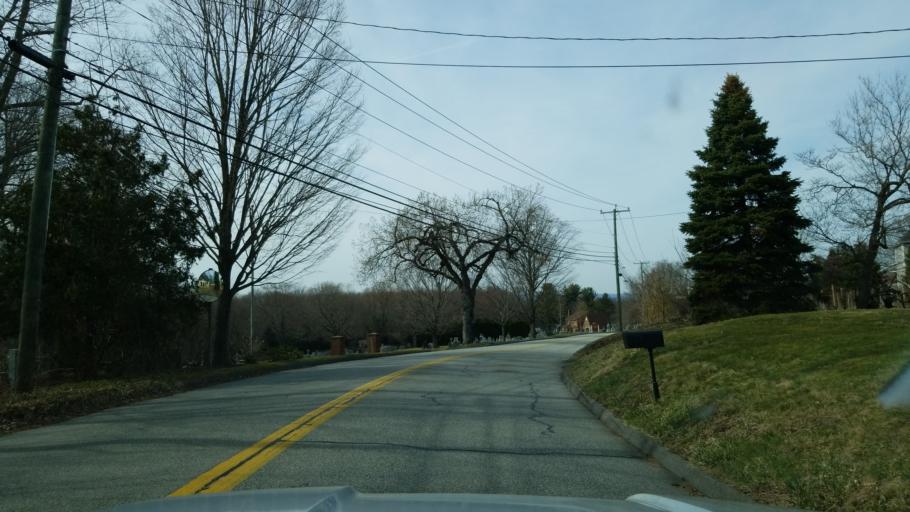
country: US
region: Connecticut
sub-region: Hartford County
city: Glastonbury Center
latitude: 41.6639
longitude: -72.5935
